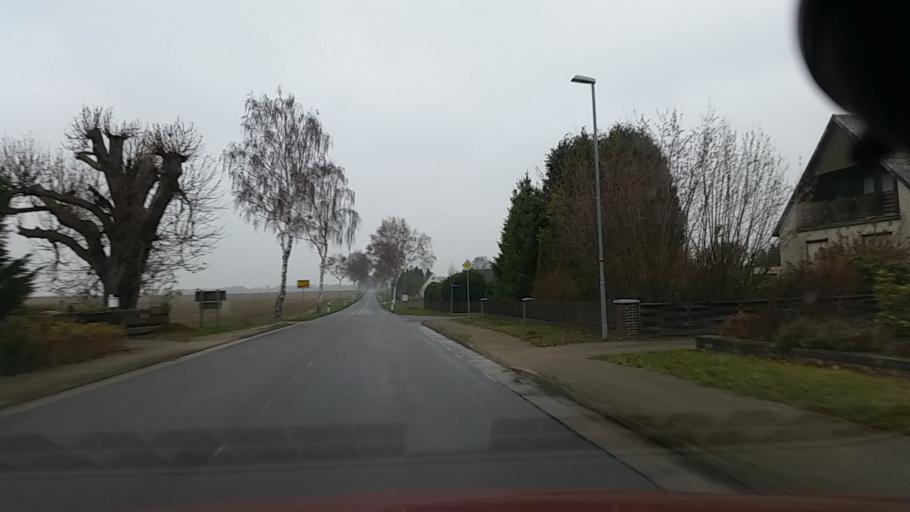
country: DE
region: Lower Saxony
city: Hankensbuttel
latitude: 52.7470
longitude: 10.6005
